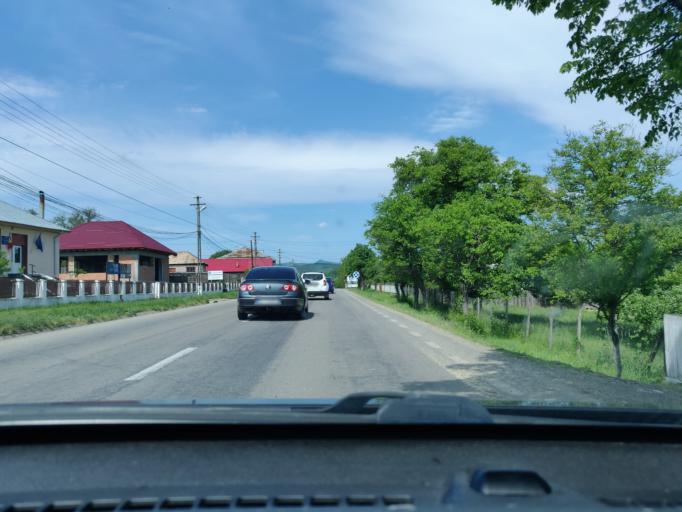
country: RO
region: Vrancea
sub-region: Comuna Vidra
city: Burca
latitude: 45.9120
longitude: 26.9475
